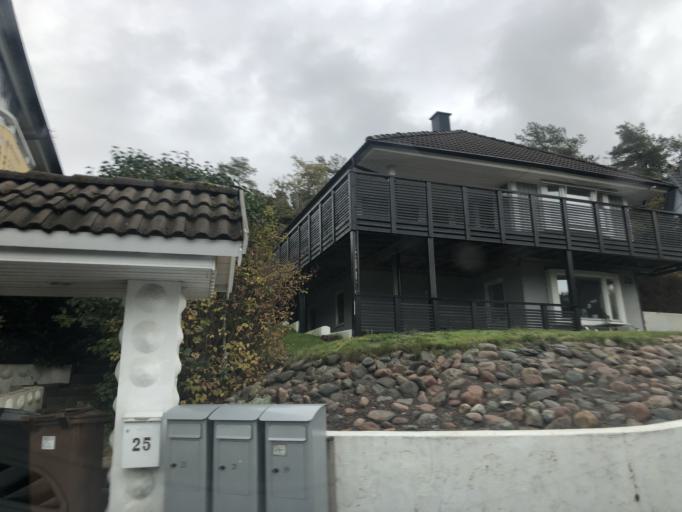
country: SE
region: Vaestra Goetaland
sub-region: Goteborg
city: Majorna
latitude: 57.6723
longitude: 11.8894
